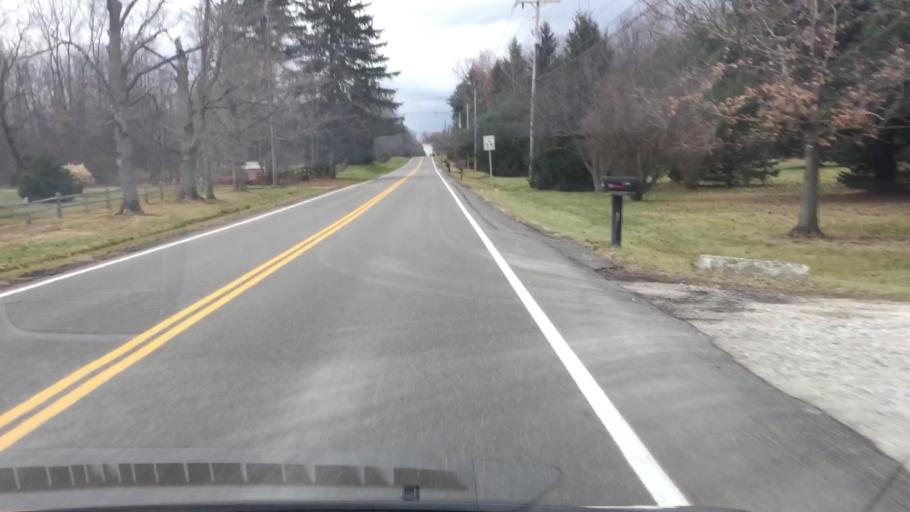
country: US
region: Ohio
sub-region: Summit County
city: Boston Heights
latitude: 41.2442
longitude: -81.5014
